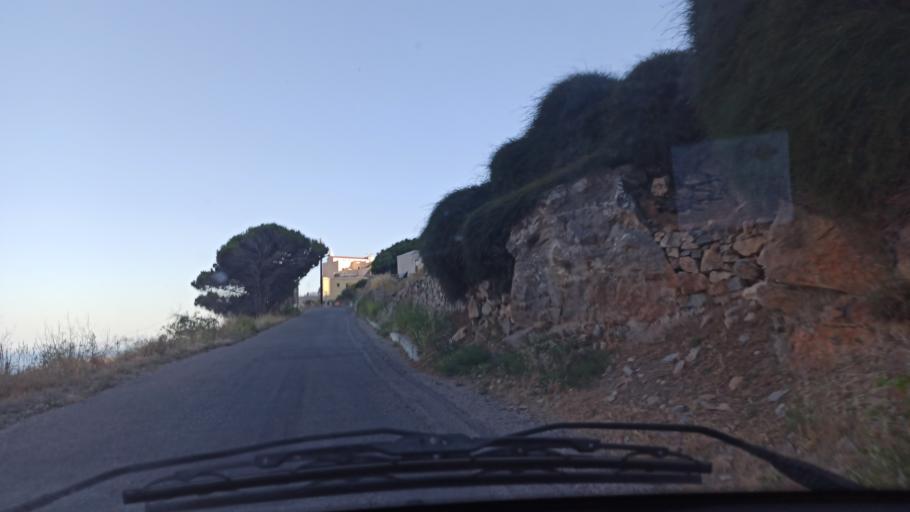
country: GR
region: South Aegean
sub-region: Nomos Kykladon
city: Ano Syros
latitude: 37.4542
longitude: 24.9348
